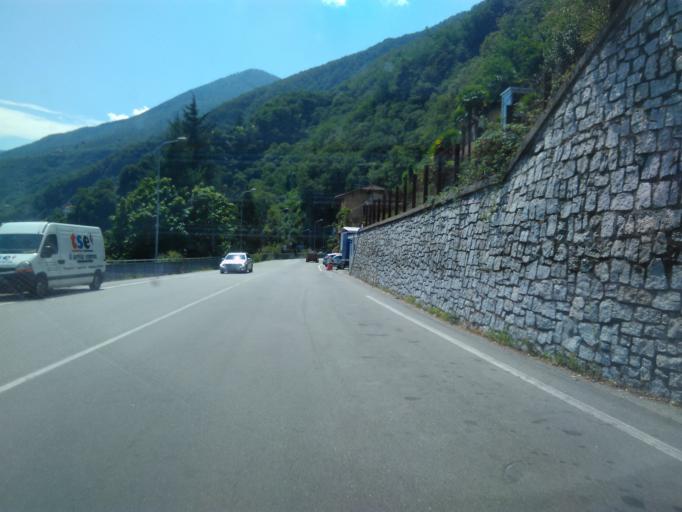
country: CH
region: Ticino
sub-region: Locarno District
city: Brissago
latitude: 46.1015
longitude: 8.6966
